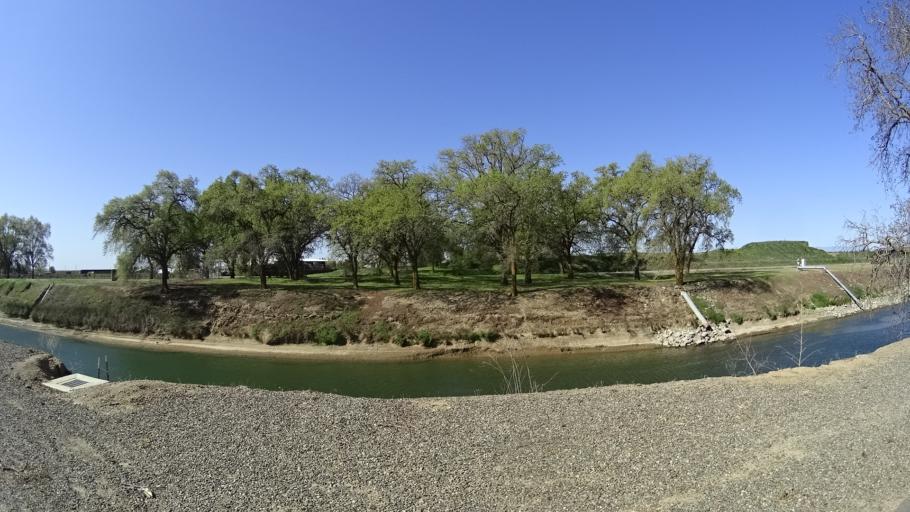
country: US
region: California
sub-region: Glenn County
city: Hamilton City
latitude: 39.7871
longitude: -122.0480
